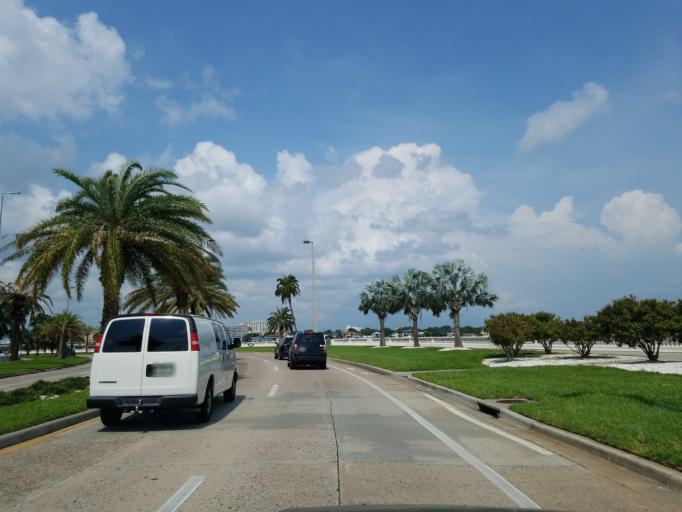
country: US
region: Florida
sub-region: Hillsborough County
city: Tampa
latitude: 27.9329
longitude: -82.4688
